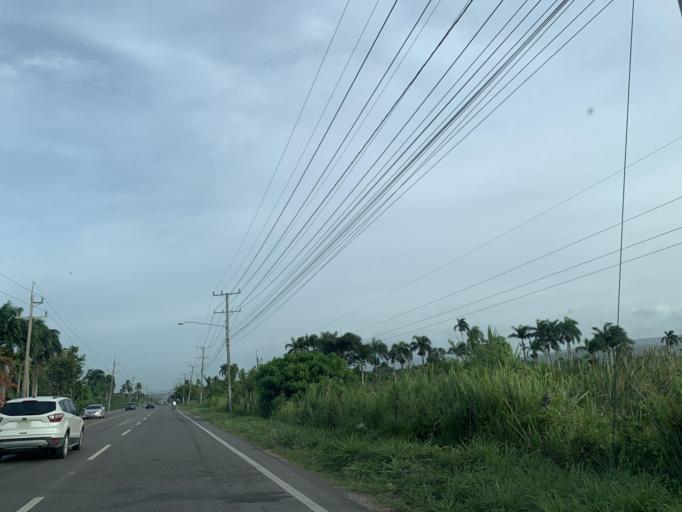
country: DO
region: Puerto Plata
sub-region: Puerto Plata
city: Puerto Plata
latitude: 19.7612
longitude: -70.6472
